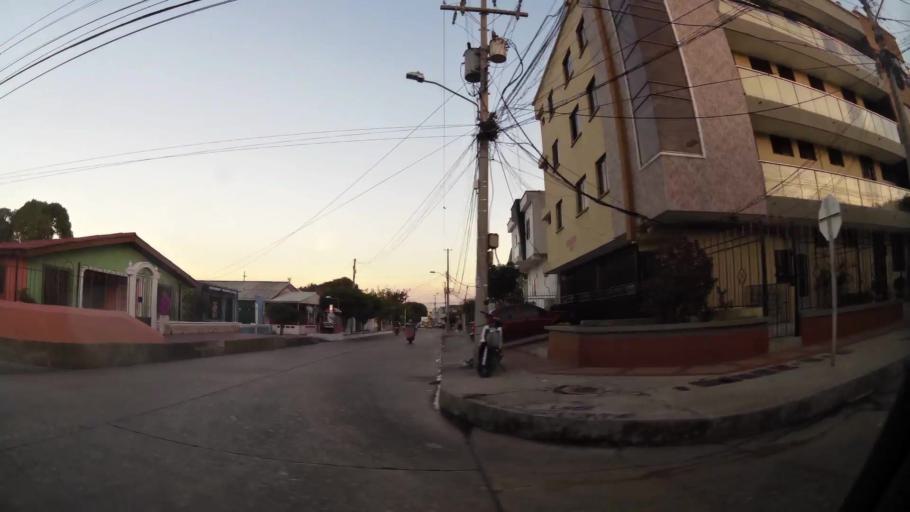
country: CO
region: Atlantico
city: Barranquilla
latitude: 10.9804
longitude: -74.8069
